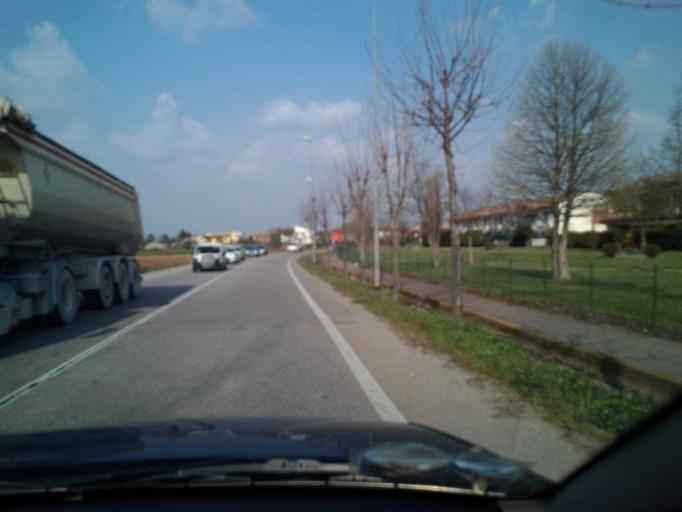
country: IT
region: Veneto
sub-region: Provincia di Verona
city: Villafranca di Verona
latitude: 45.3585
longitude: 10.8356
